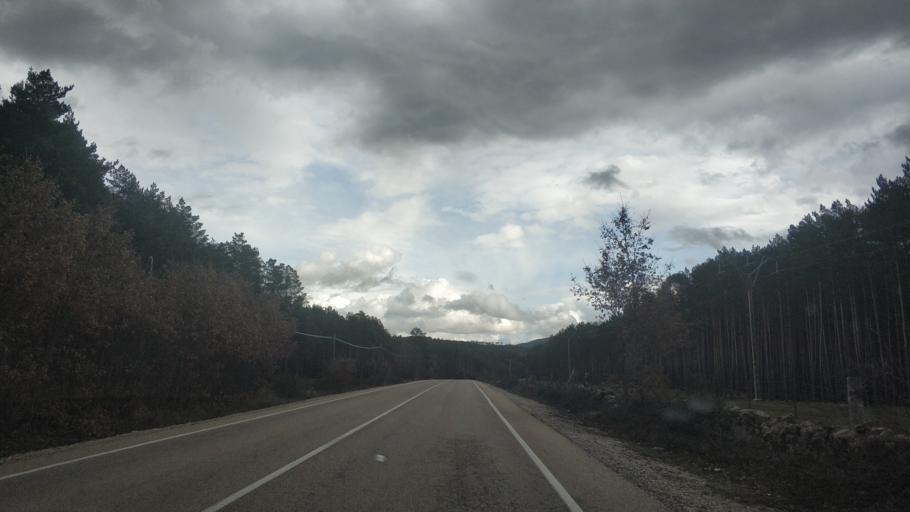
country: ES
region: Castille and Leon
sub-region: Provincia de Burgos
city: Quintanar de la Sierra
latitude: 41.9666
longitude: -3.0285
